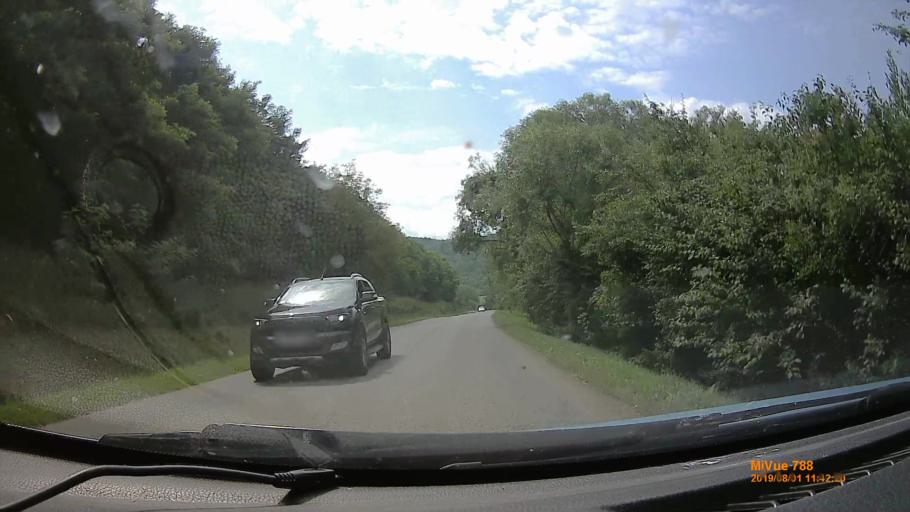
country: HU
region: Baranya
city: Villany
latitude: 45.8860
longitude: 18.4114
